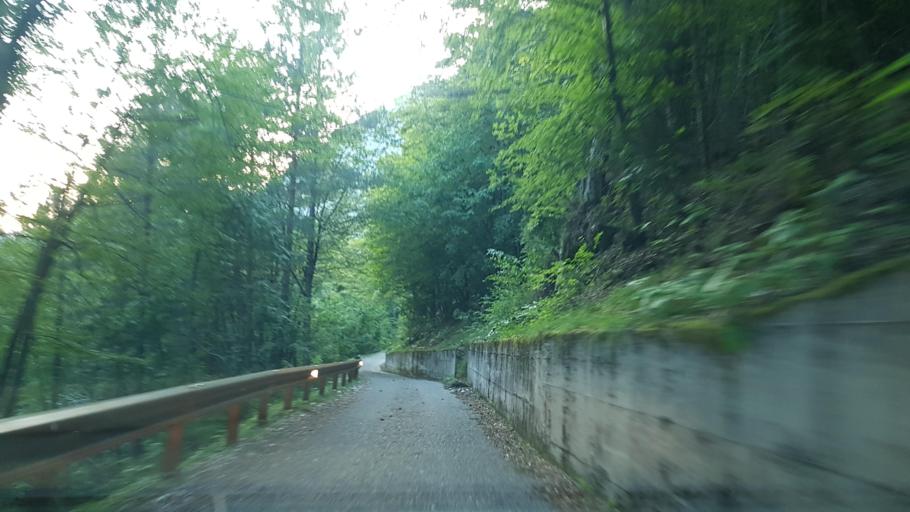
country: IT
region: Friuli Venezia Giulia
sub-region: Provincia di Udine
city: Malborghetto
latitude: 46.3992
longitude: 13.4321
